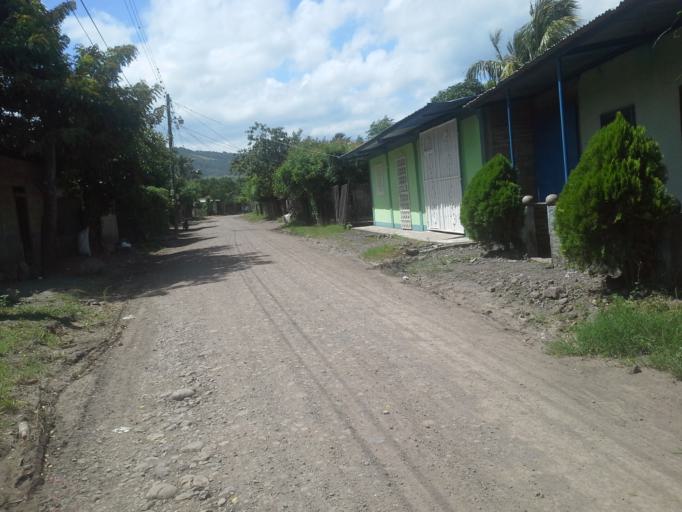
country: NI
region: Matagalpa
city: Ciudad Dario
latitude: 12.8598
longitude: -86.0985
